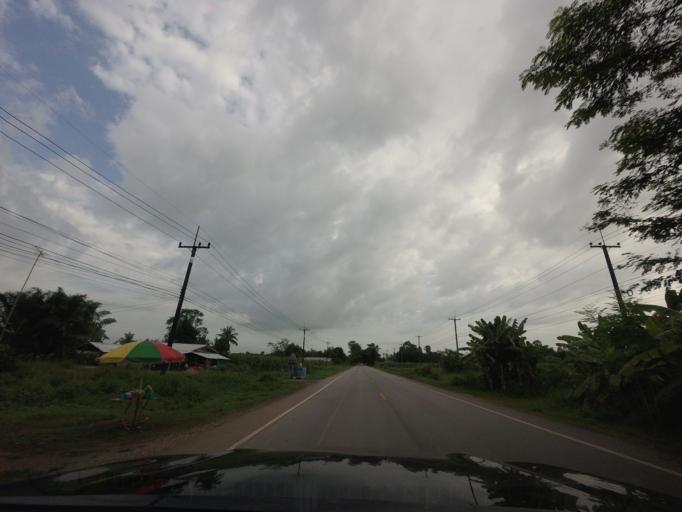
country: TH
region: Changwat Udon Thani
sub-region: Amphoe Ban Phue
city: Ban Phue
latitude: 17.7350
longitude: 102.3966
